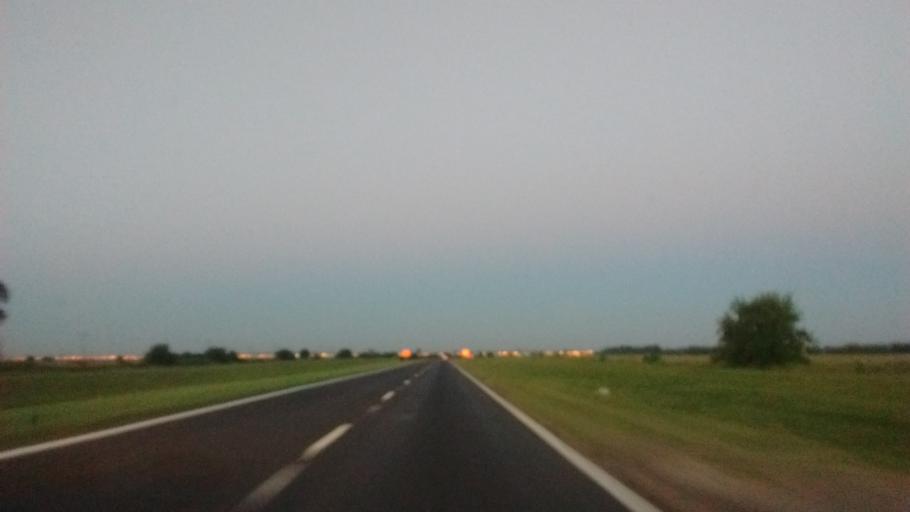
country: AR
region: Santa Fe
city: Funes
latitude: -32.9336
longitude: -60.8468
